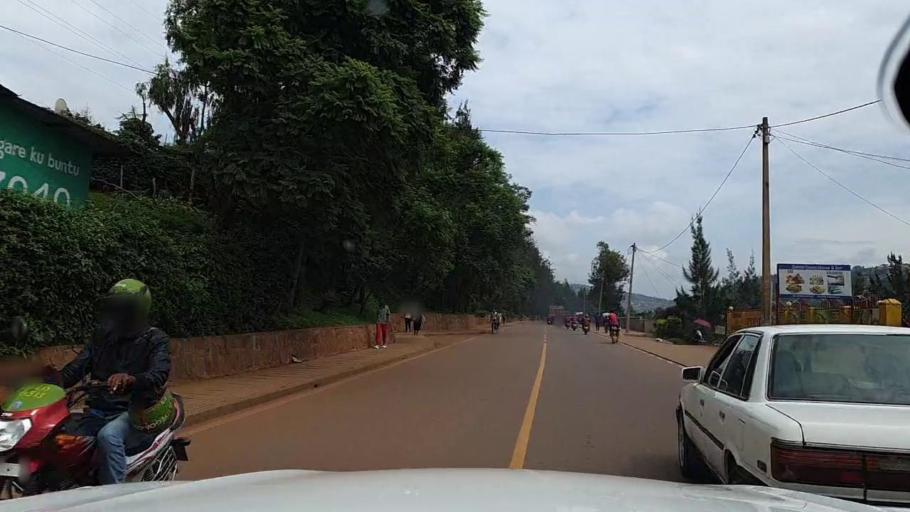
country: RW
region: Kigali
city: Kigali
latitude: -1.9316
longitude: 30.0457
